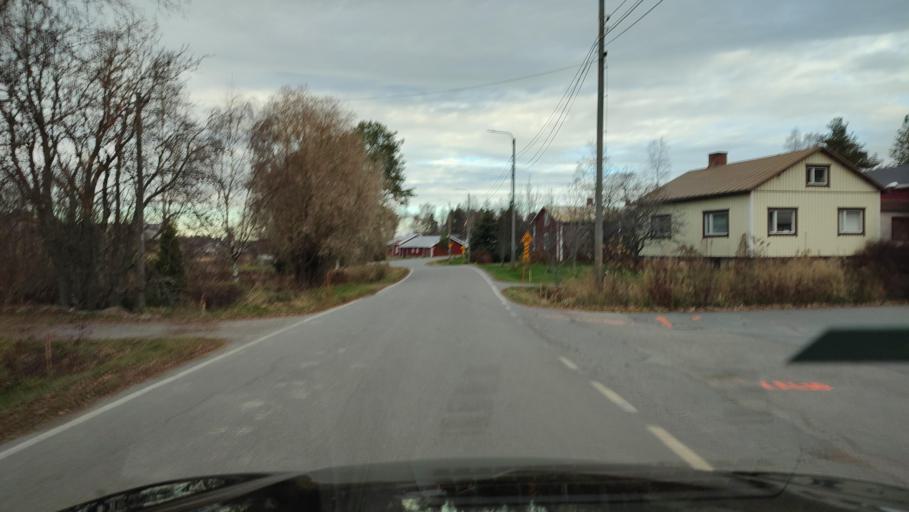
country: FI
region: Ostrobothnia
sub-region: Sydosterbotten
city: Naerpes
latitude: 62.4704
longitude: 21.3730
